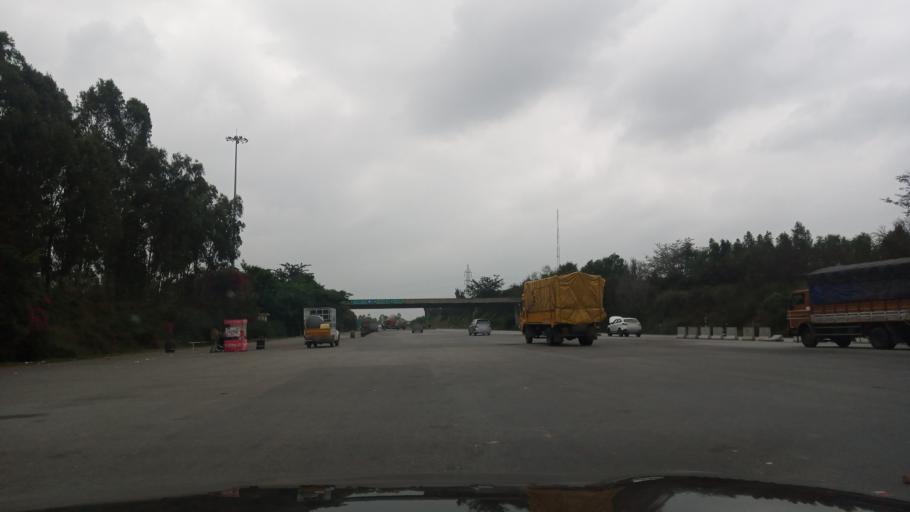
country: IN
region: Karnataka
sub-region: Bangalore Rural
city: Nelamangala
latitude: 13.0420
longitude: 77.4755
